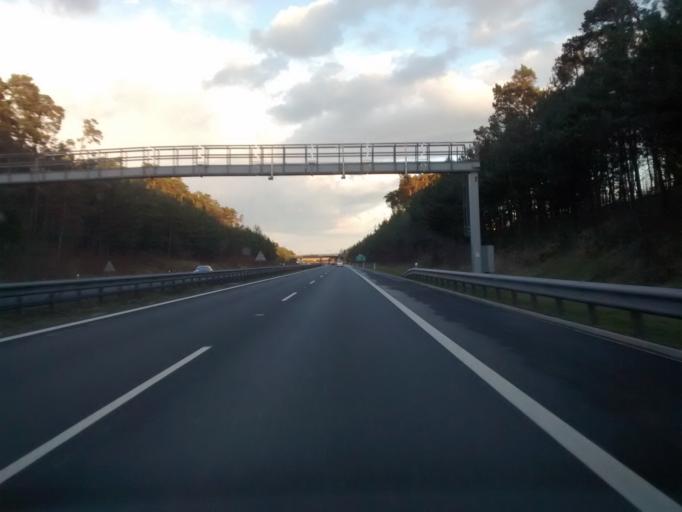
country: CZ
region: Central Bohemia
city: Poricany
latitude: 50.1210
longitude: 14.9355
